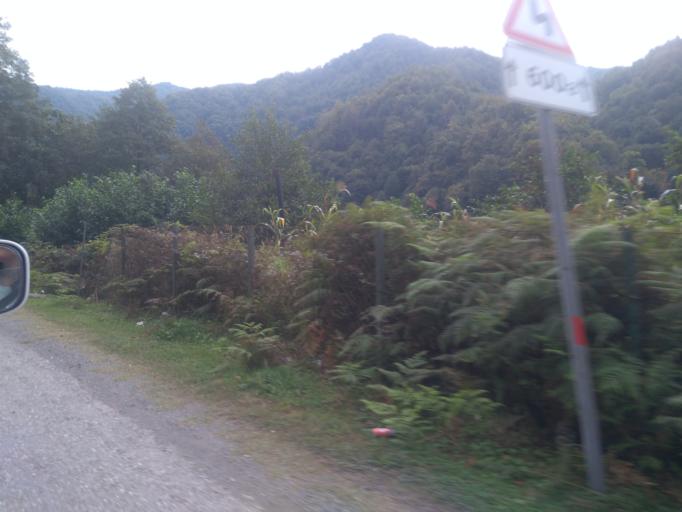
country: TR
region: Artvin
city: Muratli
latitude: 41.5455
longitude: 41.7646
